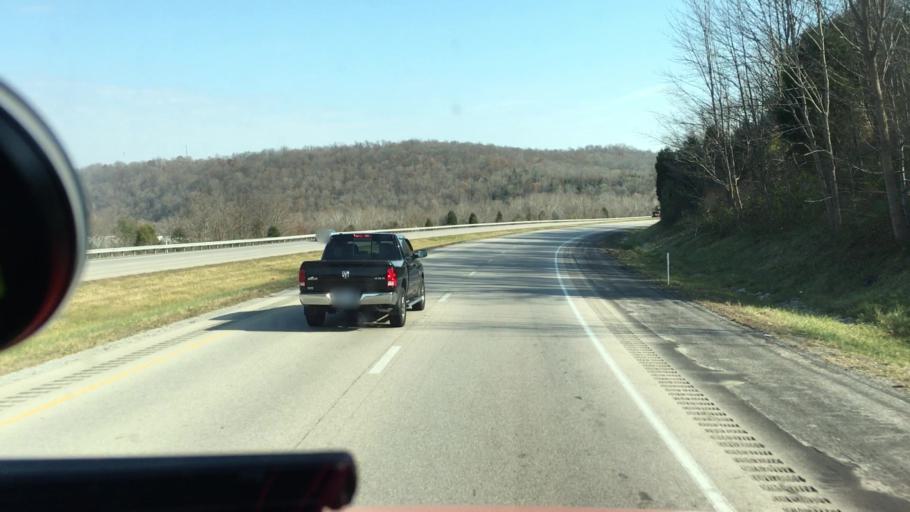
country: US
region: Kentucky
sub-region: Bath County
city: Owingsville
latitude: 38.1241
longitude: -83.7774
